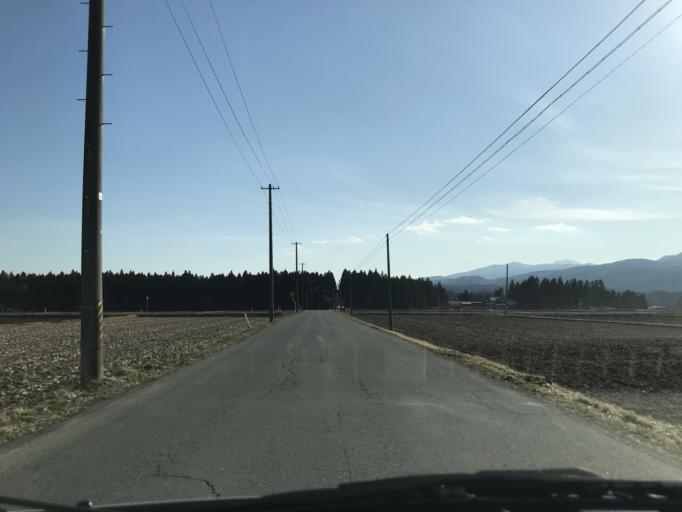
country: JP
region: Iwate
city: Kitakami
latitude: 39.3045
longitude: 141.0064
